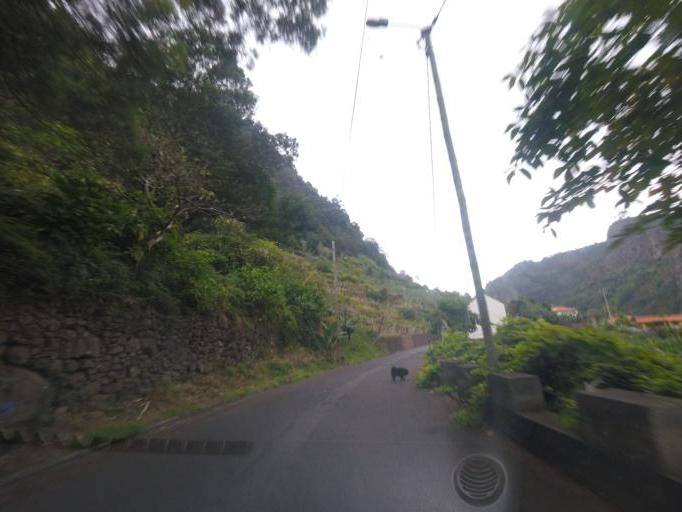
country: PT
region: Madeira
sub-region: Santana
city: Santana
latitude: 32.8192
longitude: -16.9004
